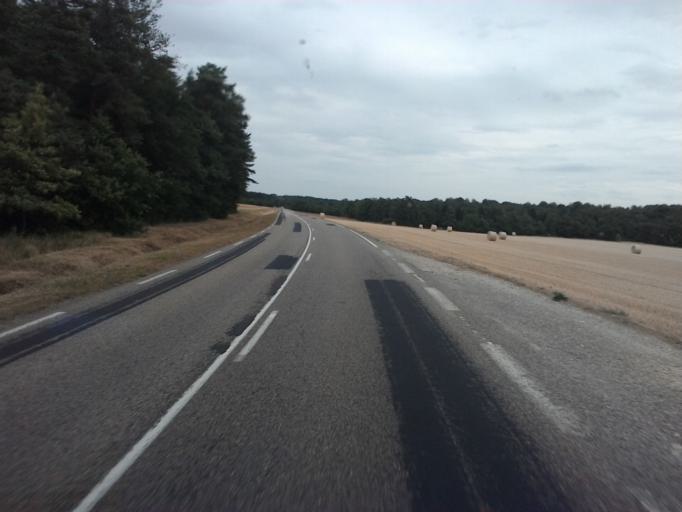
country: FR
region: Lorraine
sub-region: Departement de Meurthe-et-Moselle
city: Colombey-les-Belles
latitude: 48.5578
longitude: 5.9299
